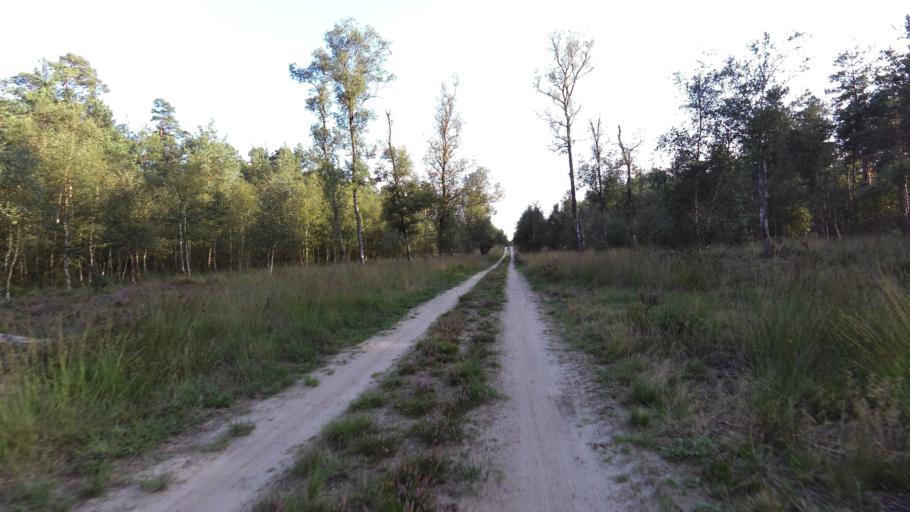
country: NL
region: Gelderland
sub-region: Gemeente Epe
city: Vaassen
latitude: 52.2830
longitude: 5.8765
